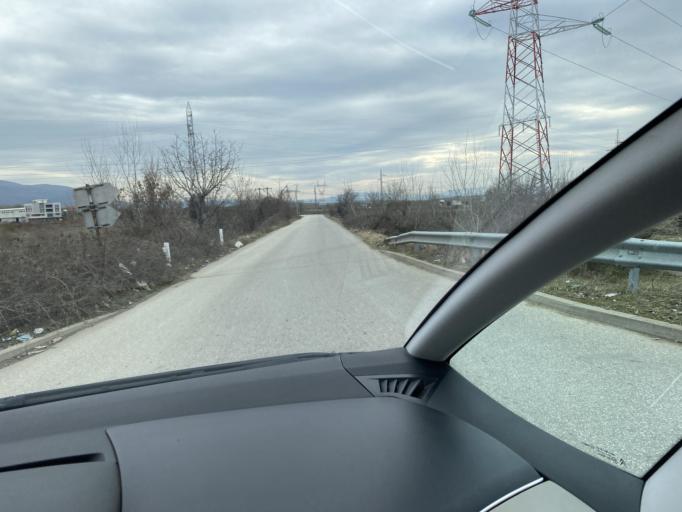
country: MK
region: Butel
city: Butel
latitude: 42.0421
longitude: 21.4553
